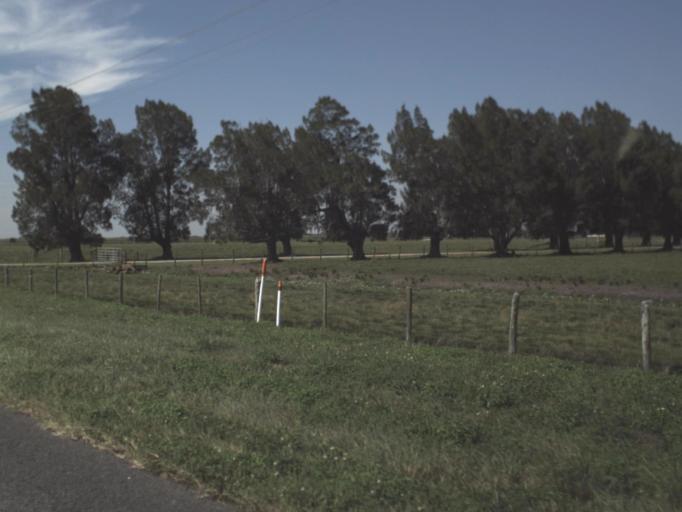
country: US
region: Florida
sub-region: Hendry County
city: Harlem
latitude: 26.7542
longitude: -81.0137
